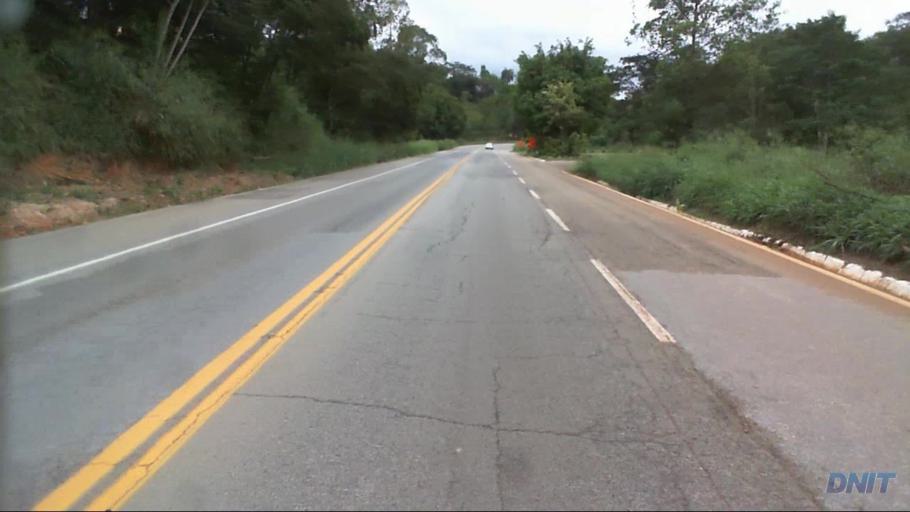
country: BR
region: Minas Gerais
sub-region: Barao De Cocais
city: Barao de Cocais
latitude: -19.7977
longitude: -43.4222
